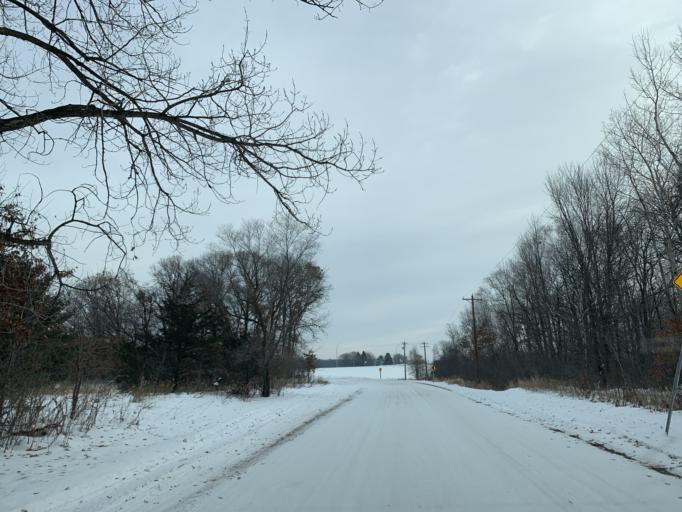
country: US
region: Minnesota
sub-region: Washington County
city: Forest Lake
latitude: 45.2901
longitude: -93.0079
